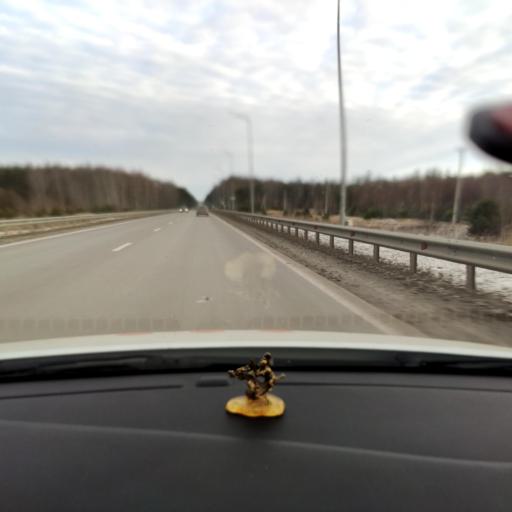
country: RU
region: Tatarstan
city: Stolbishchi
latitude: 55.6455
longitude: 49.1277
